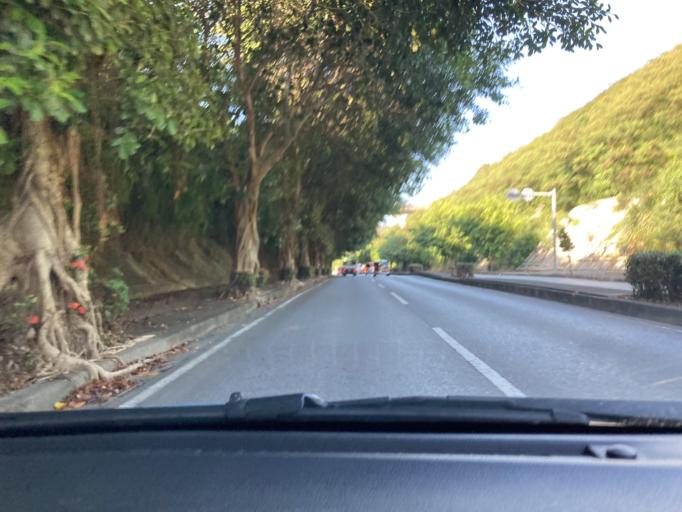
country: JP
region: Okinawa
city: Tomigusuku
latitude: 26.1745
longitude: 127.7121
